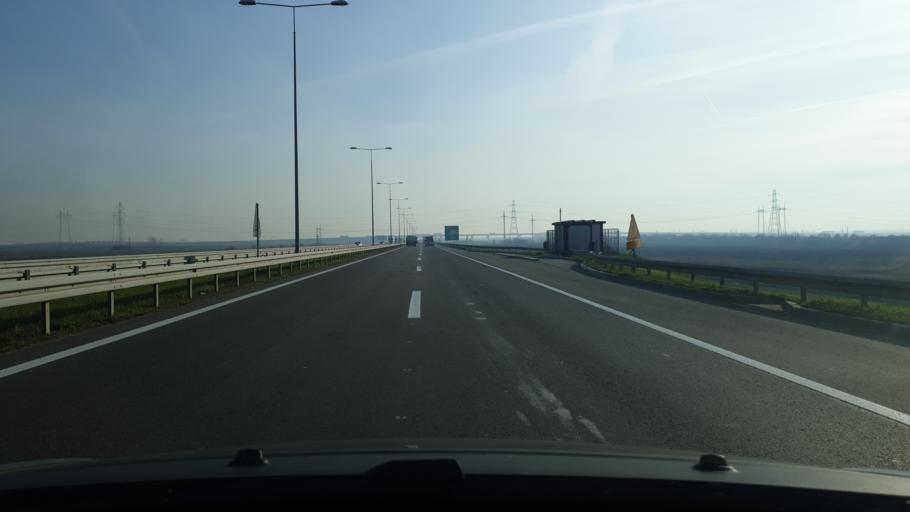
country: RS
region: Central Serbia
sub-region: Belgrade
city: Surcin
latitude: 44.7822
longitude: 20.2639
